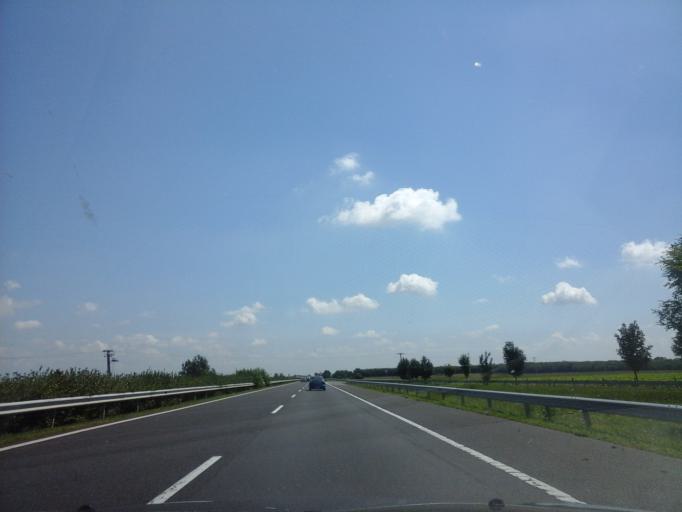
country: HU
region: Borsod-Abauj-Zemplen
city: Hejobaba
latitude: 47.8790
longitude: 20.9042
